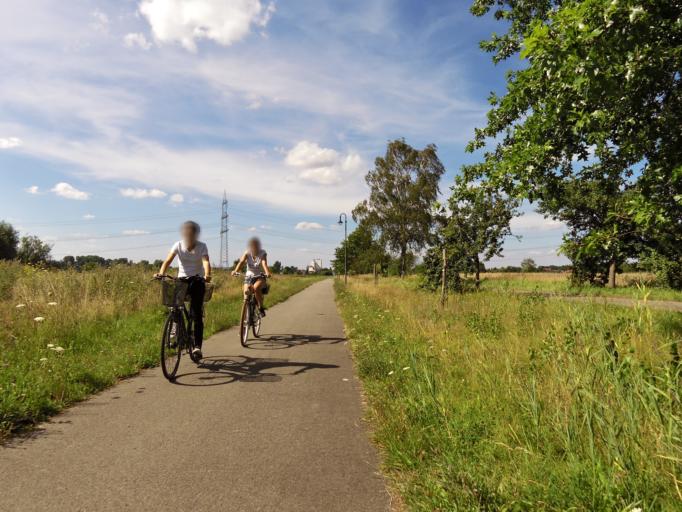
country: DE
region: Rheinland-Pfalz
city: Bohl-Iggelheim
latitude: 49.3507
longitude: 8.3203
